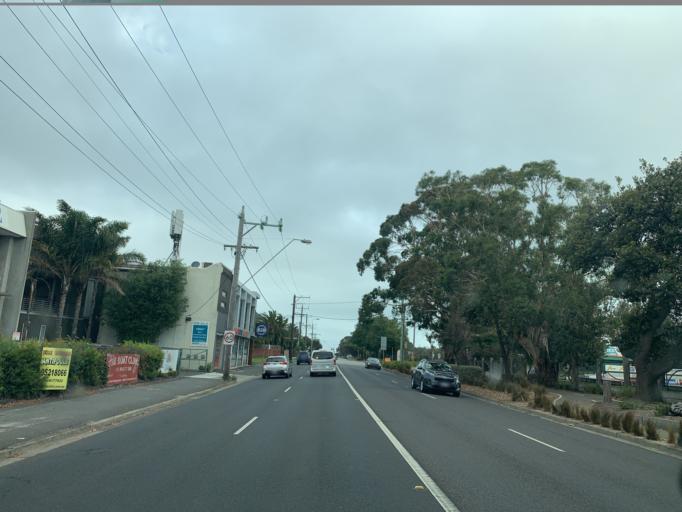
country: AU
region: Victoria
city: Hampton
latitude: -37.9449
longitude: 145.0012
